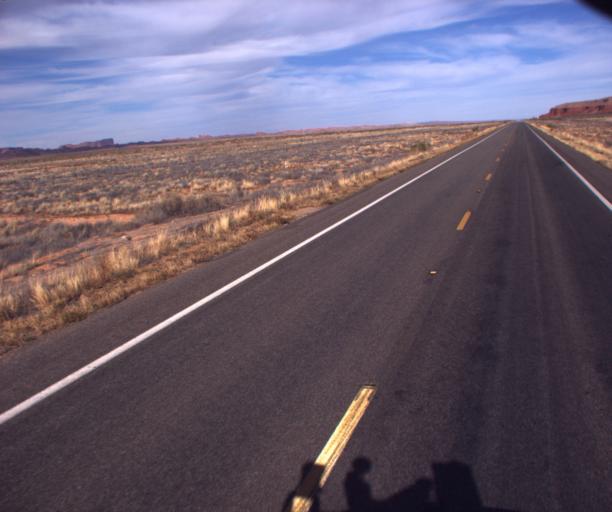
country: US
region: Arizona
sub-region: Navajo County
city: Kayenta
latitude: 36.7523
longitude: -110.0590
